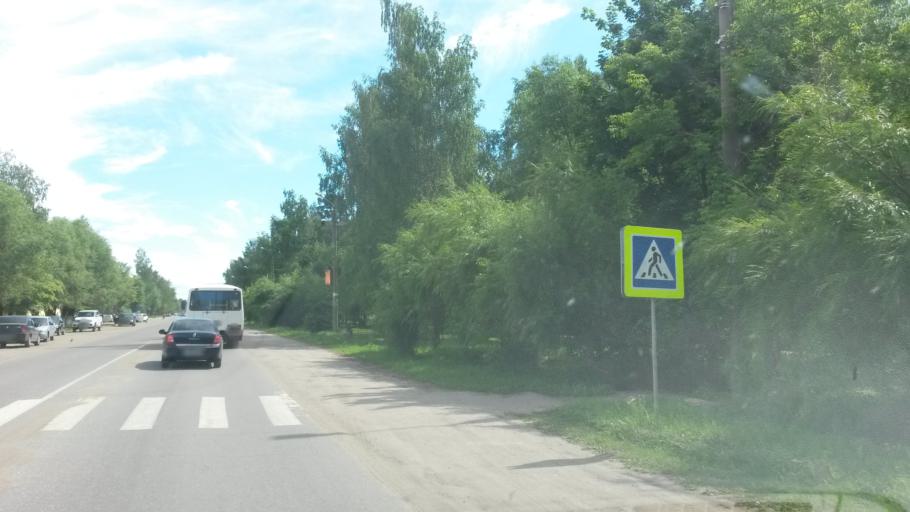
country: RU
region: Ivanovo
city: Zavolzhsk
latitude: 57.4886
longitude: 42.1406
